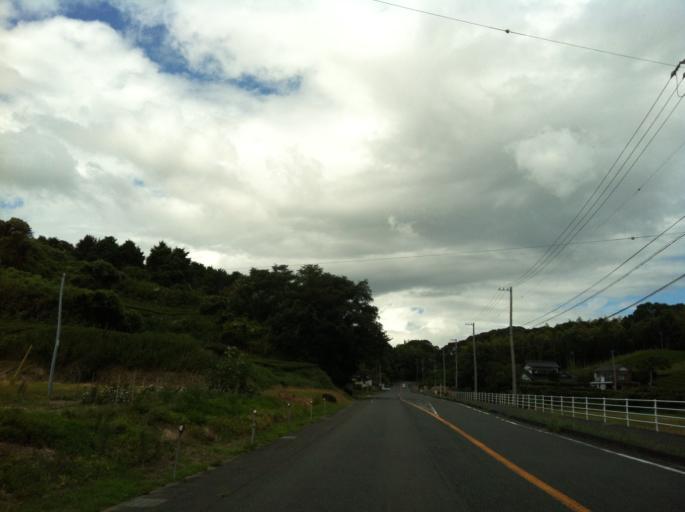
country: JP
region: Shizuoka
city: Kakegawa
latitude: 34.6857
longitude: 138.0427
